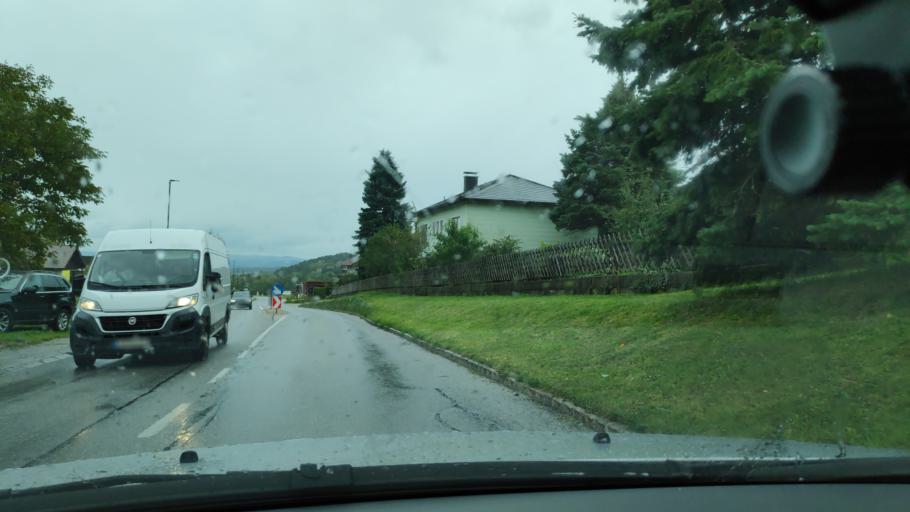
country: AT
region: Lower Austria
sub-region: Politischer Bezirk Neunkirchen
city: Willendorf am Steinfelde
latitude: 47.7940
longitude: 16.0379
